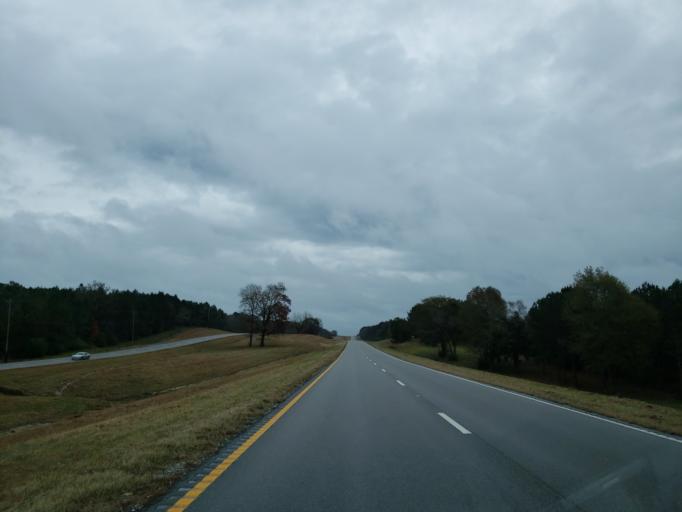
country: US
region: Mississippi
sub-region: Wayne County
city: Waynesboro
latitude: 31.6950
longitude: -88.7623
